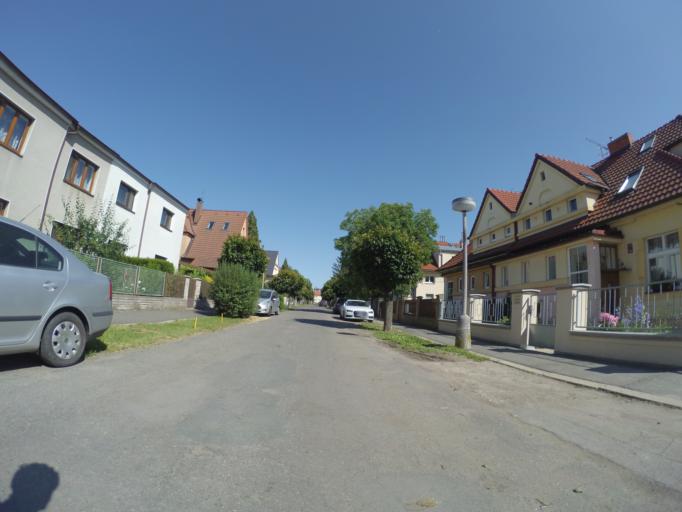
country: CZ
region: Central Bohemia
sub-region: Okres Nymburk
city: Podebrady
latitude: 50.1509
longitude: 15.1157
